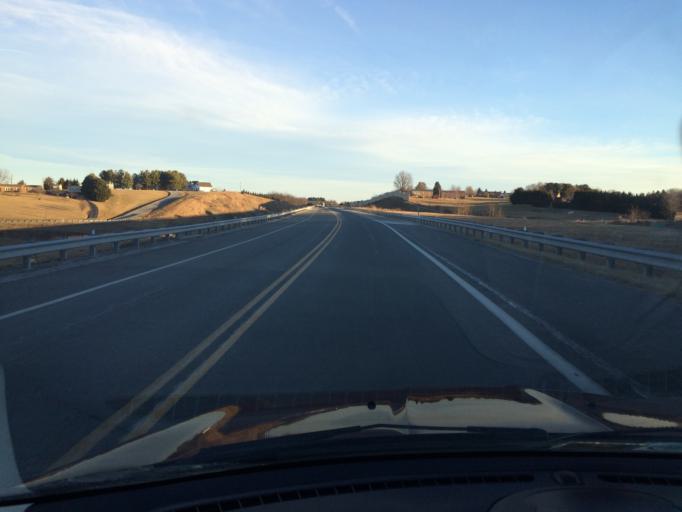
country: US
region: Virginia
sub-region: City of Staunton
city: Staunton
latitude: 38.1598
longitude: -79.1115
